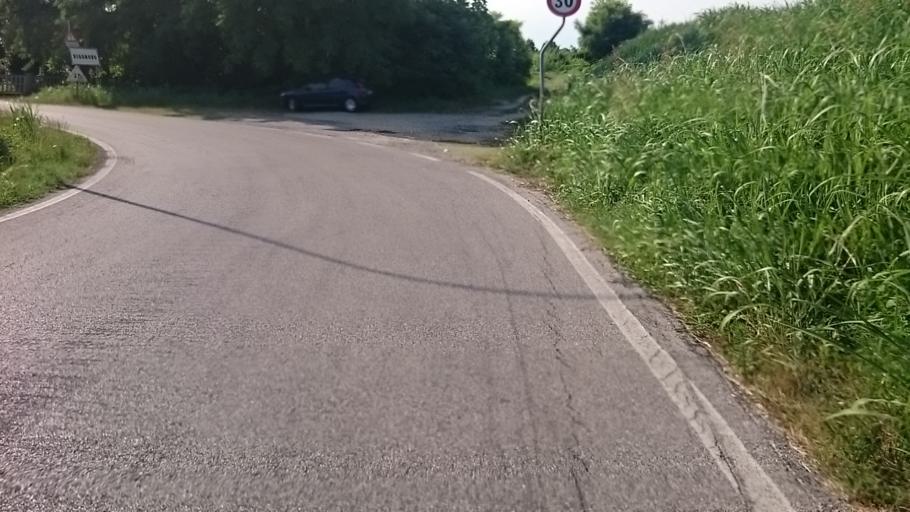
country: IT
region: Veneto
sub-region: Provincia di Venezia
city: Vigonovo
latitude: 45.3861
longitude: 12.0154
